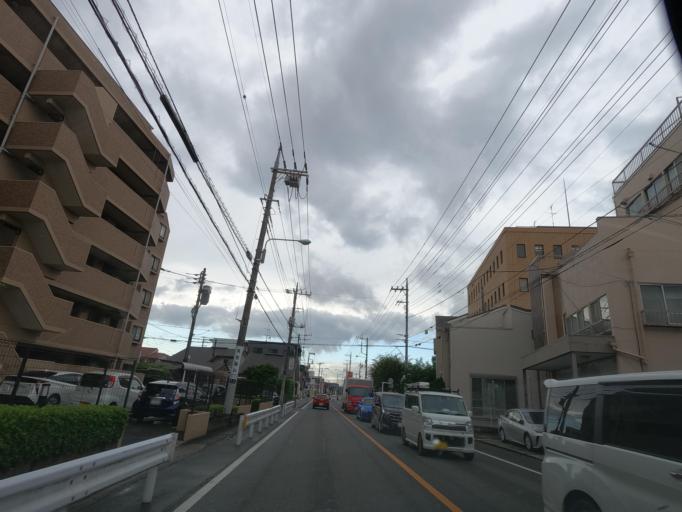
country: JP
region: Saitama
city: Yono
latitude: 35.8772
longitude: 139.6563
